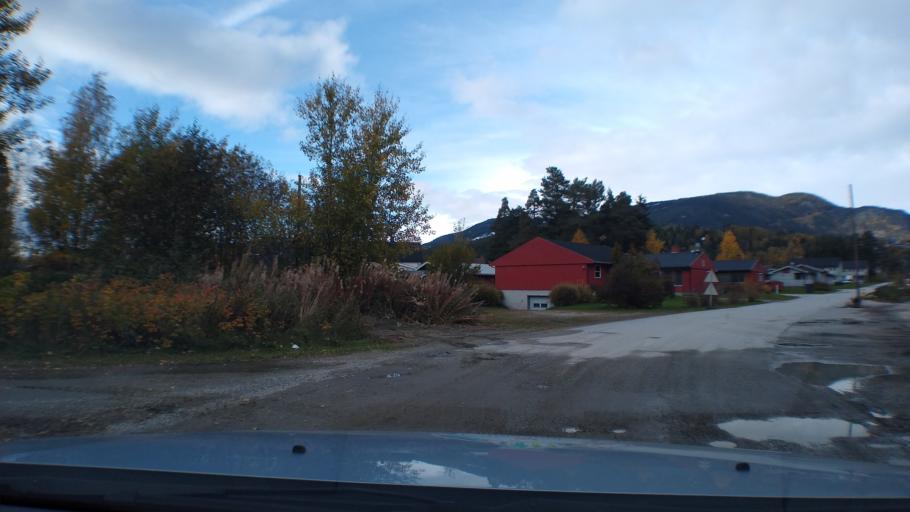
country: NO
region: Oppland
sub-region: Ringebu
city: Ringebu
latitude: 61.5255
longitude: 10.1362
